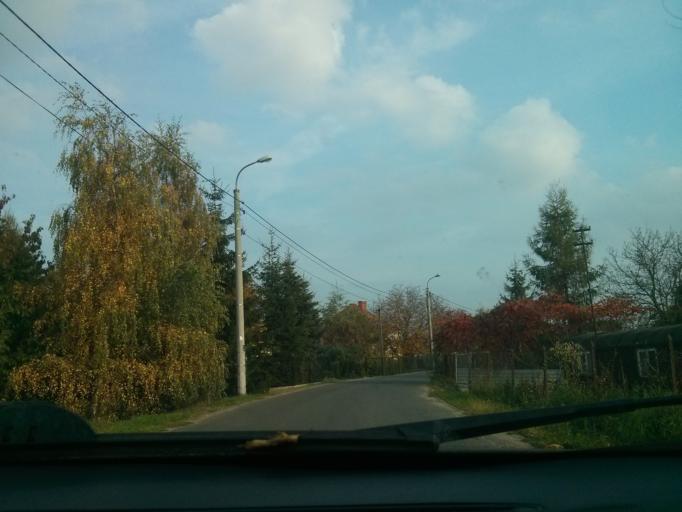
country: PL
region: Masovian Voivodeship
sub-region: Powiat piaseczynski
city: Konstancin-Jeziorna
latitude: 52.1359
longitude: 21.1516
